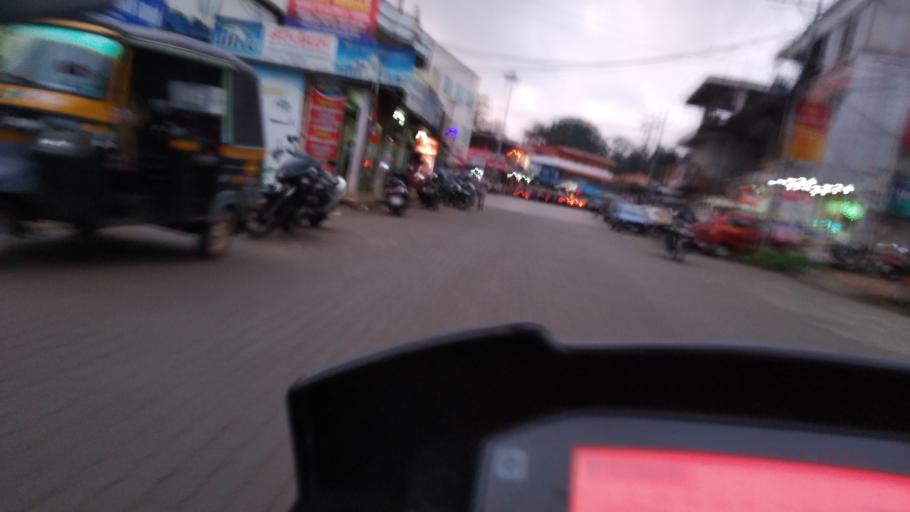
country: IN
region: Kerala
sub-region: Idukki
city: Munnar
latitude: 9.9632
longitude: 77.0987
